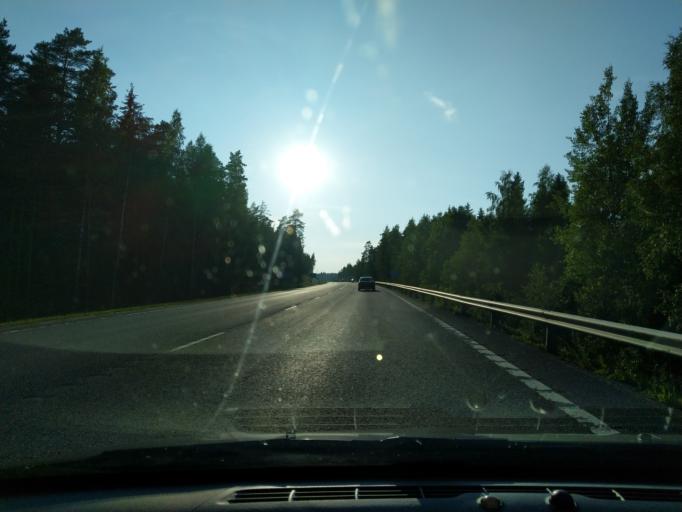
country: FI
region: Paijanne Tavastia
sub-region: Lahti
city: Lahti
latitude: 60.9659
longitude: 25.7415
